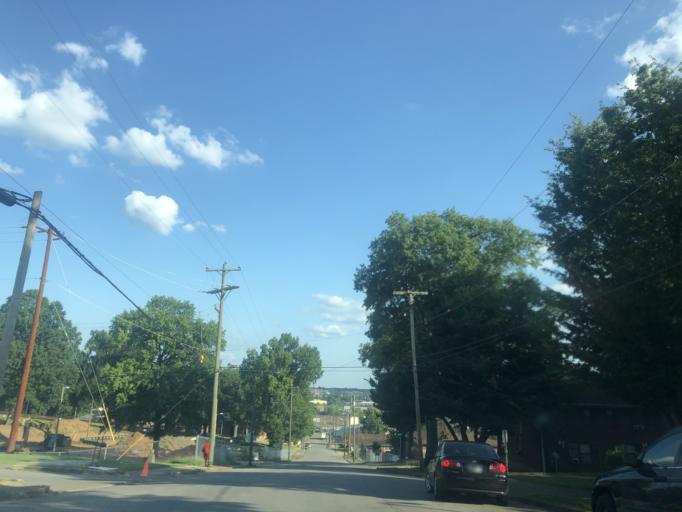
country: US
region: Tennessee
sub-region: Davidson County
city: Nashville
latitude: 36.1662
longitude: -86.7561
